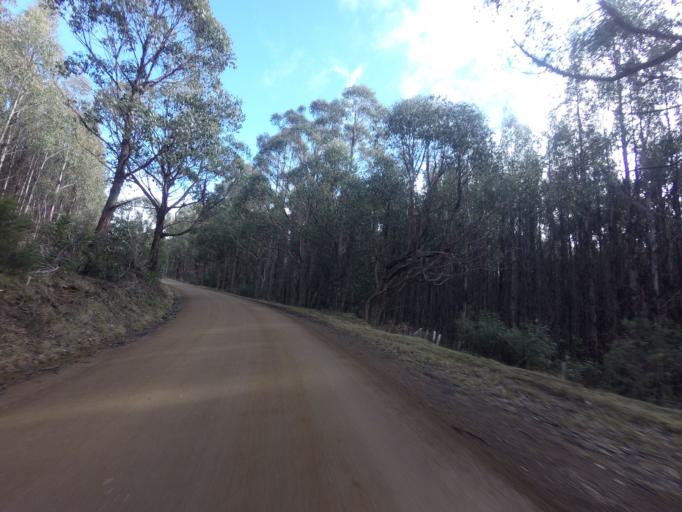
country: AU
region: Tasmania
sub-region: Derwent Valley
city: New Norfolk
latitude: -42.7845
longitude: 146.9115
